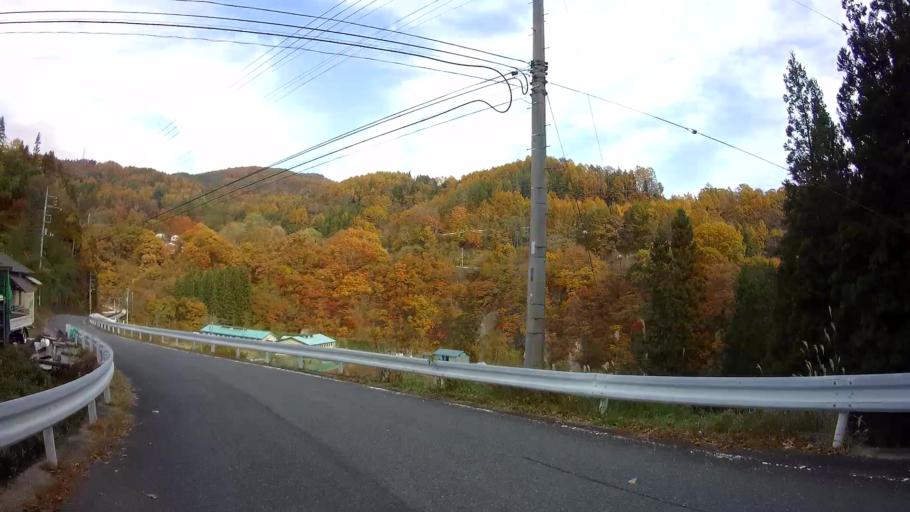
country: JP
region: Gunma
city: Nakanojomachi
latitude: 36.6378
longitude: 138.6485
